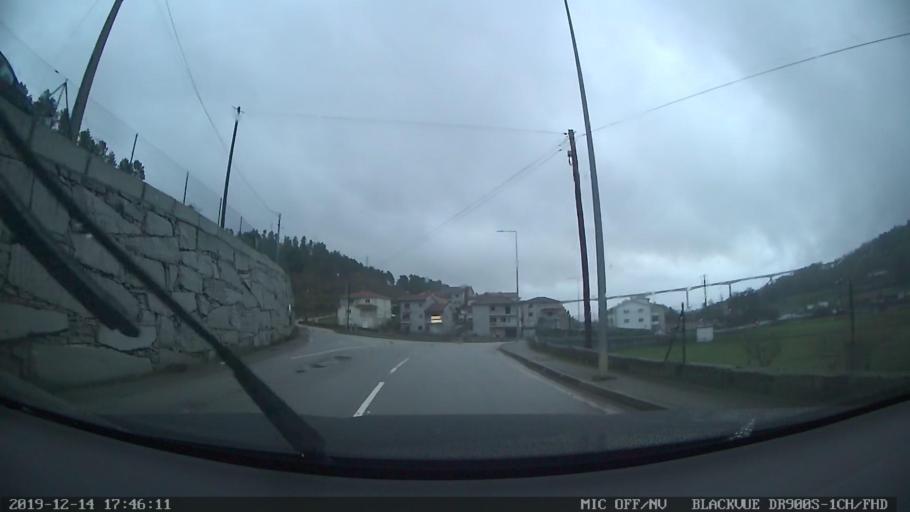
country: PT
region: Vila Real
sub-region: Vila Pouca de Aguiar
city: Vila Pouca de Aguiar
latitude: 41.4915
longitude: -7.6461
